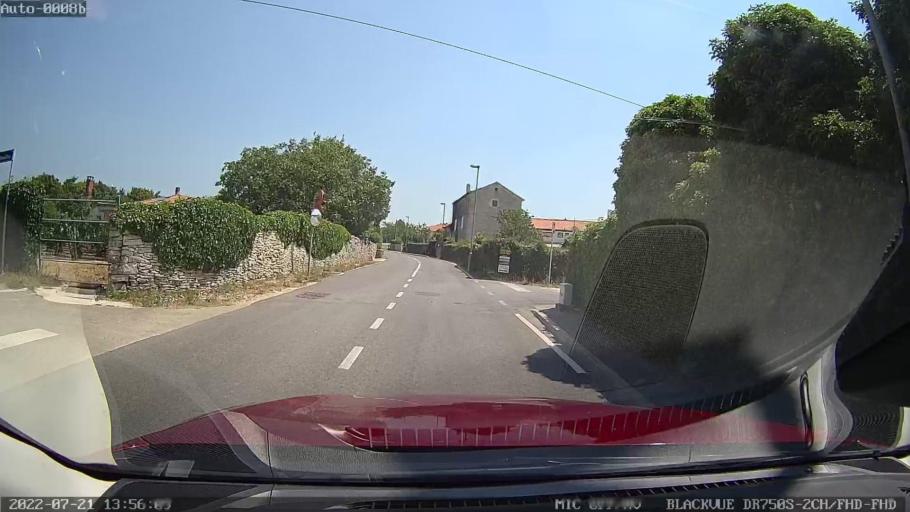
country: HR
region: Istarska
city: Pazin
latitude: 45.1207
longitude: 13.8402
